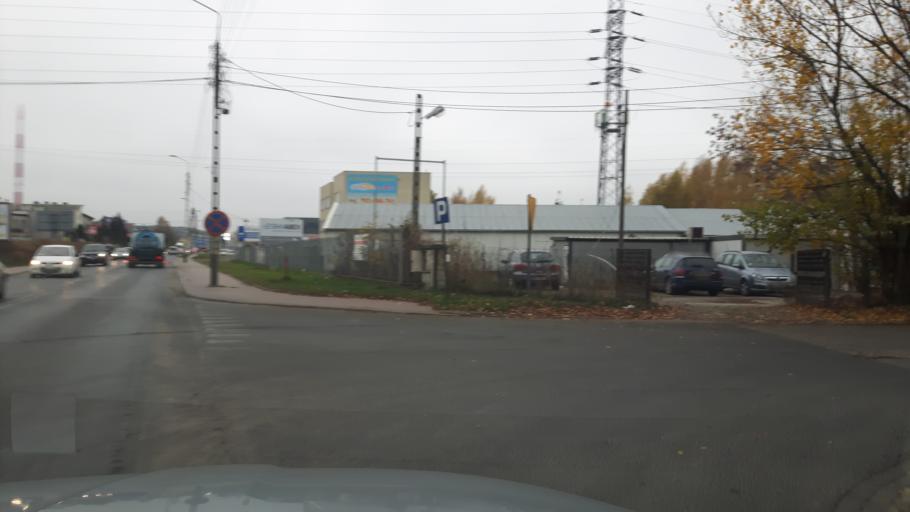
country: PL
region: Masovian Voivodeship
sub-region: Powiat wolominski
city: Zabki
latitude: 52.2805
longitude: 21.1127
